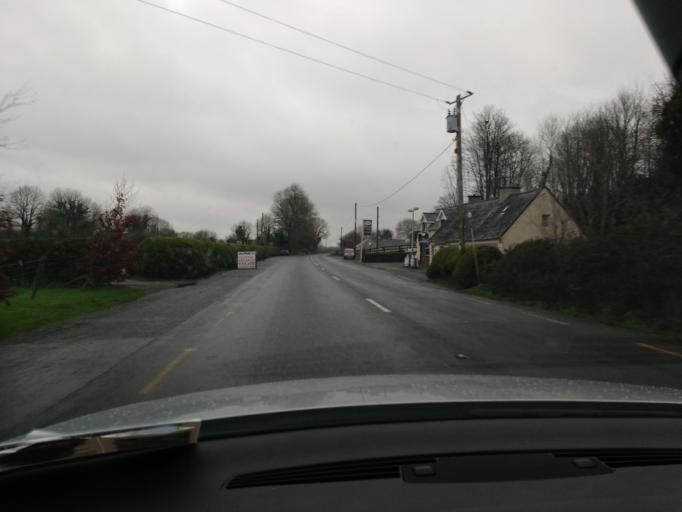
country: IE
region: Munster
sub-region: North Tipperary
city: Nenagh
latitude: 52.8165
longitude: -8.0692
